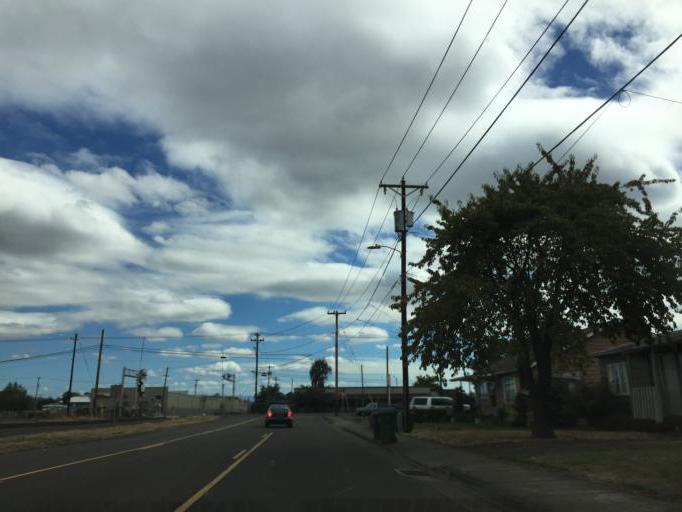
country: US
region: Oregon
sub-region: Marion County
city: Woodburn
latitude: 45.1362
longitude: -122.8461
